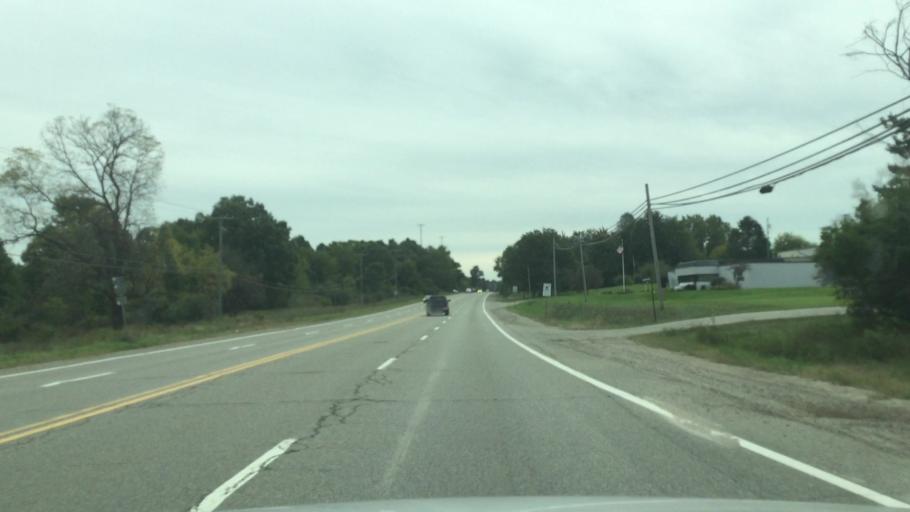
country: US
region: Michigan
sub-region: Oakland County
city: Ortonville
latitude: 42.7803
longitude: -83.4990
